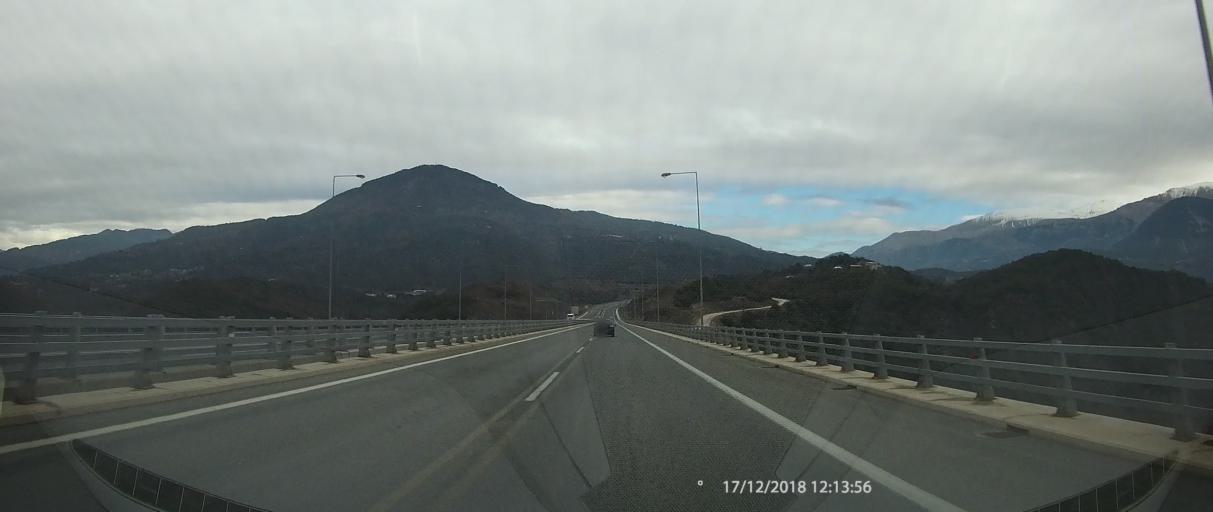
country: GR
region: Epirus
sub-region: Nomos Ioanninon
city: Katsikas
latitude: 39.7128
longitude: 20.9838
